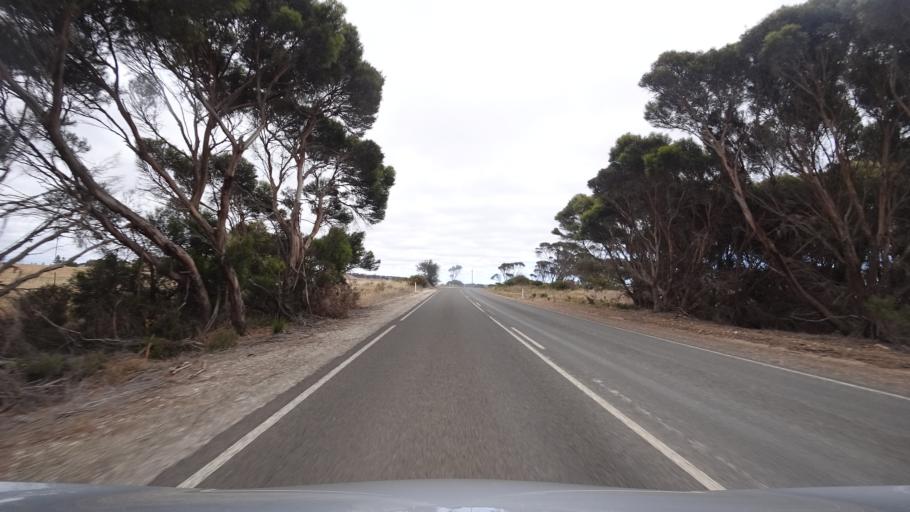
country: AU
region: South Australia
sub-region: Kangaroo Island
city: Kingscote
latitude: -35.6266
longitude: 137.5428
